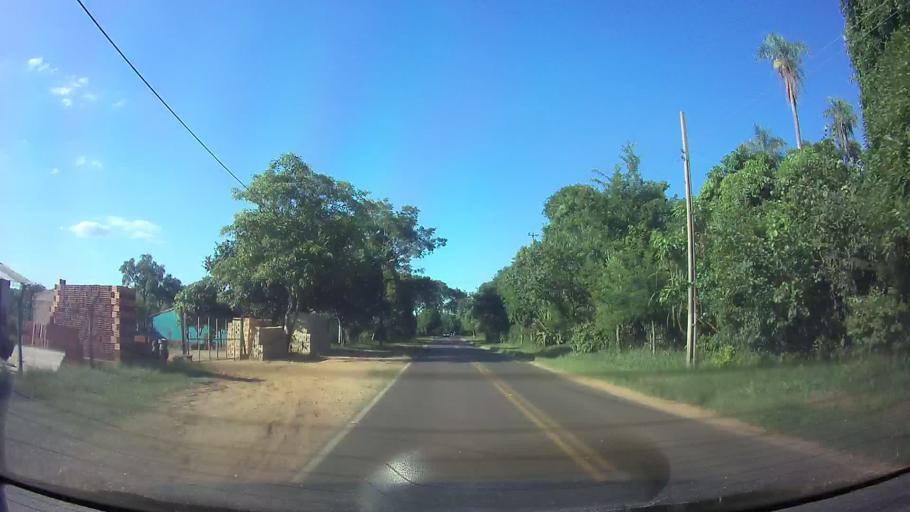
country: PY
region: Cordillera
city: Atyra
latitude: -25.2972
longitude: -57.1849
